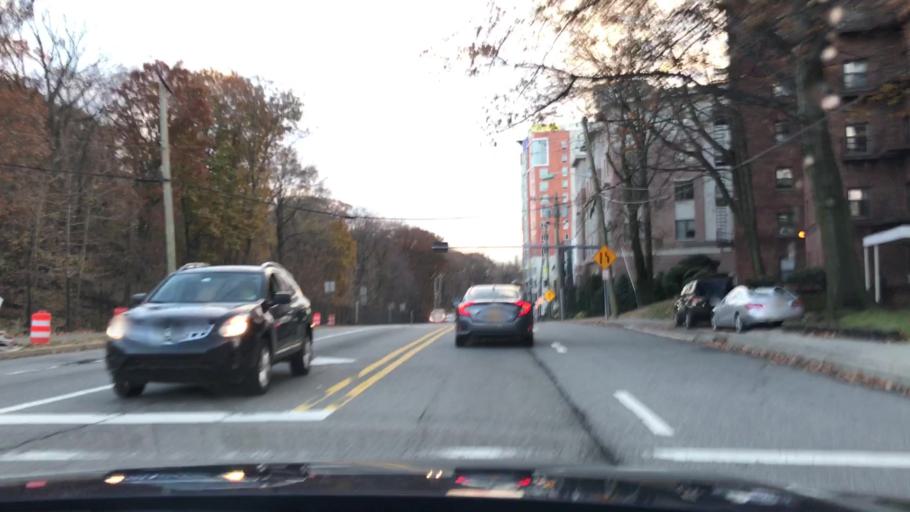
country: US
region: New Jersey
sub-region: Bergen County
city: Fort Lee
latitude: 40.8517
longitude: -73.9644
